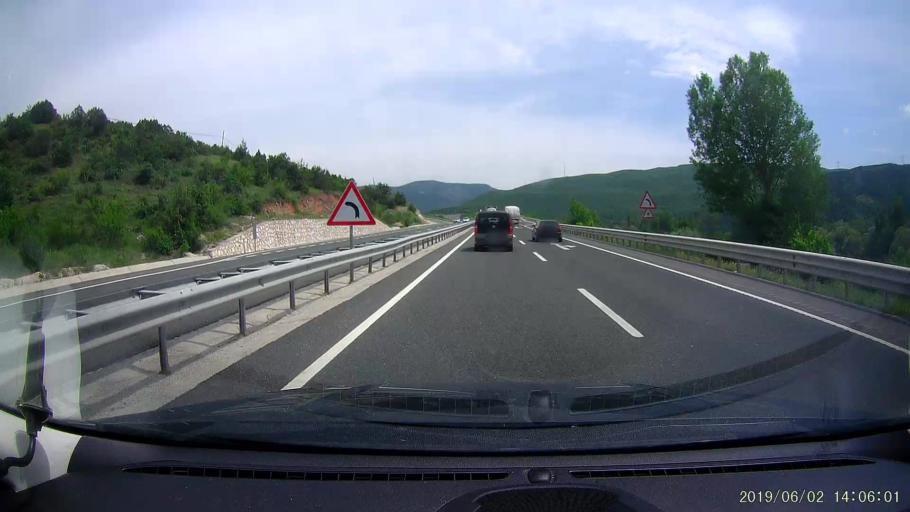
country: TR
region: Cankiri
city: Ilgaz
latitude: 40.8940
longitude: 33.6763
